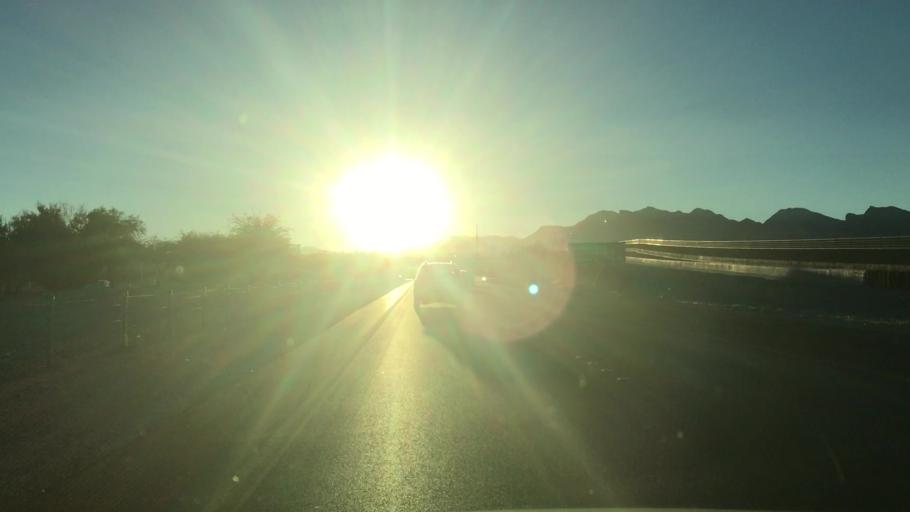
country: US
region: Nevada
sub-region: Clark County
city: Spring Valley
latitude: 36.1783
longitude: -115.2736
